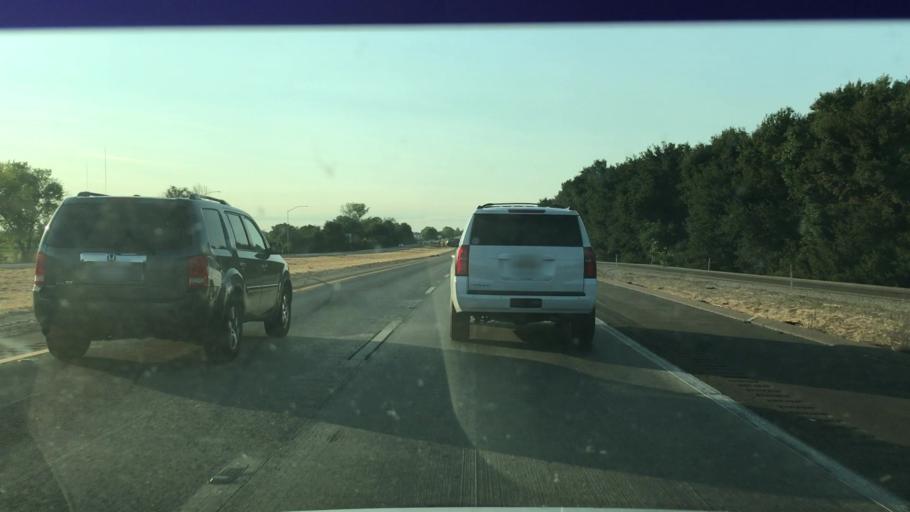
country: US
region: California
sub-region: San Joaquin County
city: Thornton
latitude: 38.2276
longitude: -121.4316
